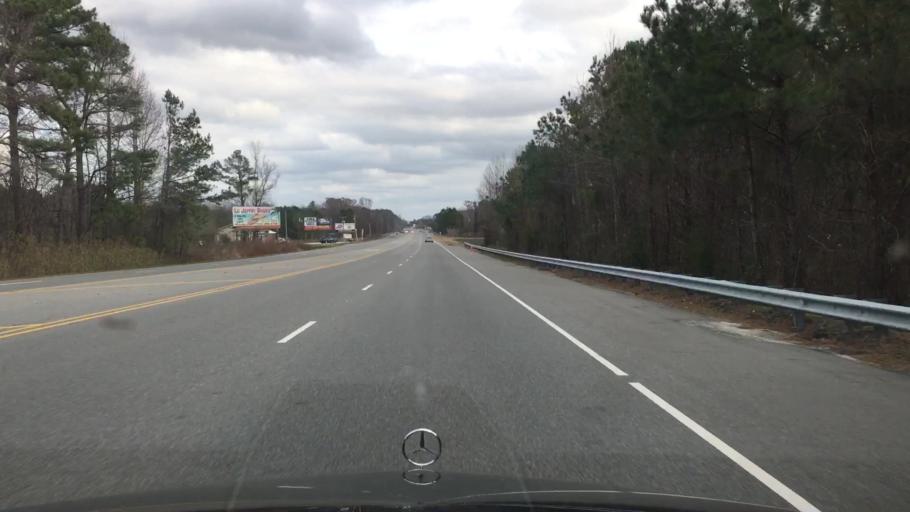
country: US
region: North Carolina
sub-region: Duplin County
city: Beulaville
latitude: 34.9290
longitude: -77.8088
